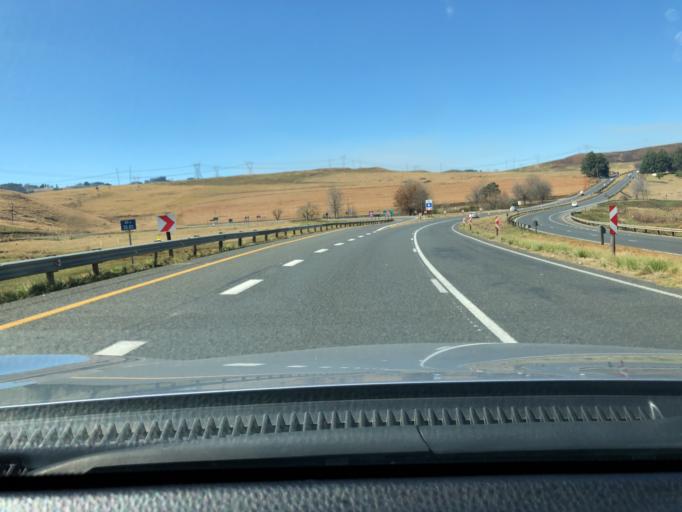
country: ZA
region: KwaZulu-Natal
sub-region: uMgungundlovu District Municipality
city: Howick
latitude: -29.4171
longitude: 30.1630
